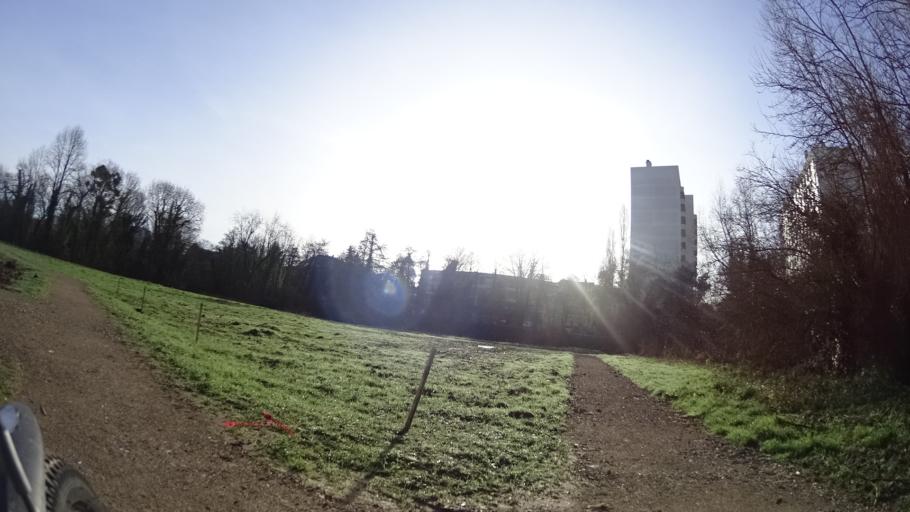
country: FR
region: Brittany
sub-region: Departement d'Ille-et-Vilaine
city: Rennes
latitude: 48.1217
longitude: -1.6768
